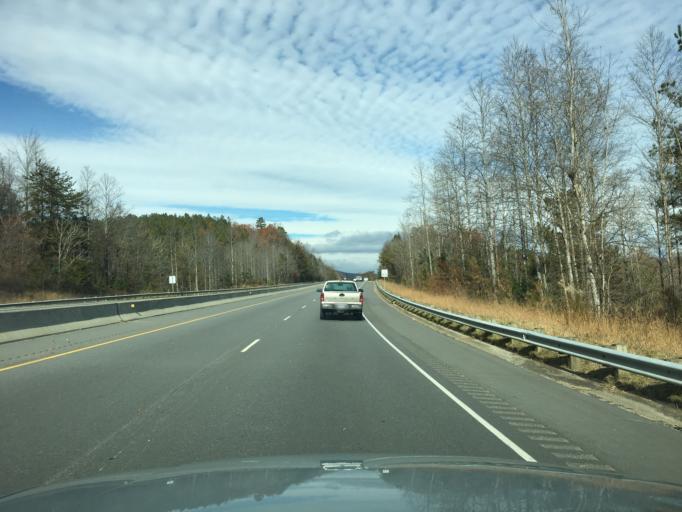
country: US
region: North Carolina
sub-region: McDowell County
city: Marion
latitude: 35.6876
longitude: -82.0305
